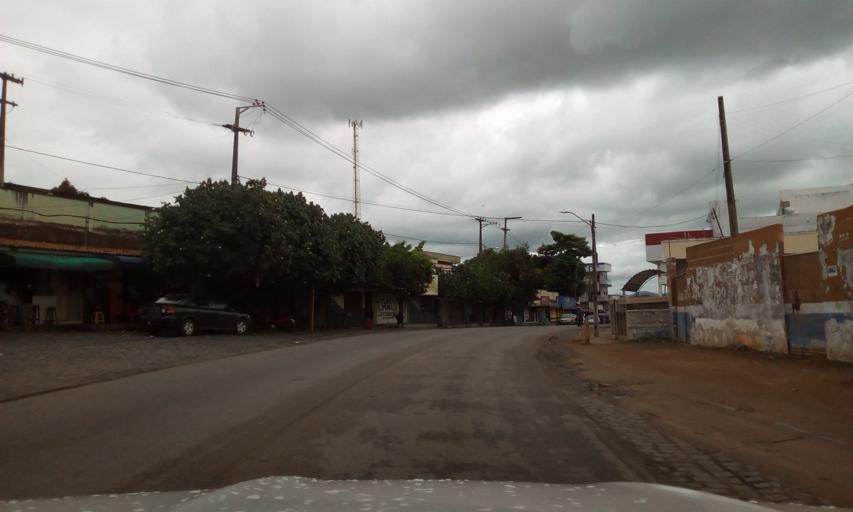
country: BR
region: Paraiba
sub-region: Guarabira
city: Guarabira
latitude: -6.8478
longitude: -35.4891
